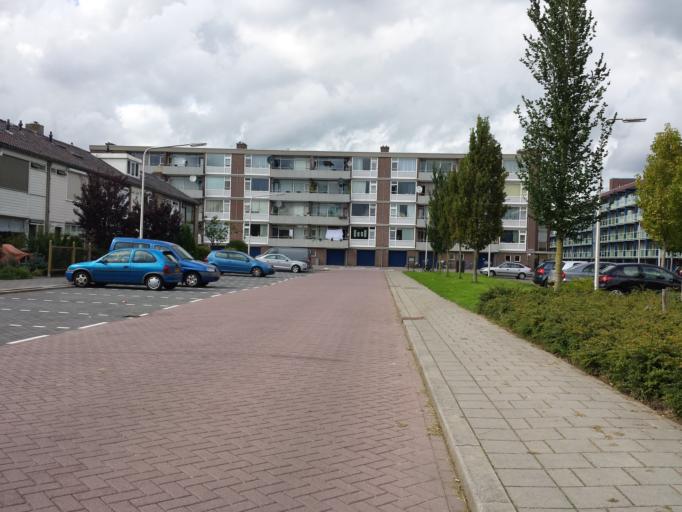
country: NL
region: South Holland
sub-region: Gemeente Gouda
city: Gouda
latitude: 52.0129
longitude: 4.7334
